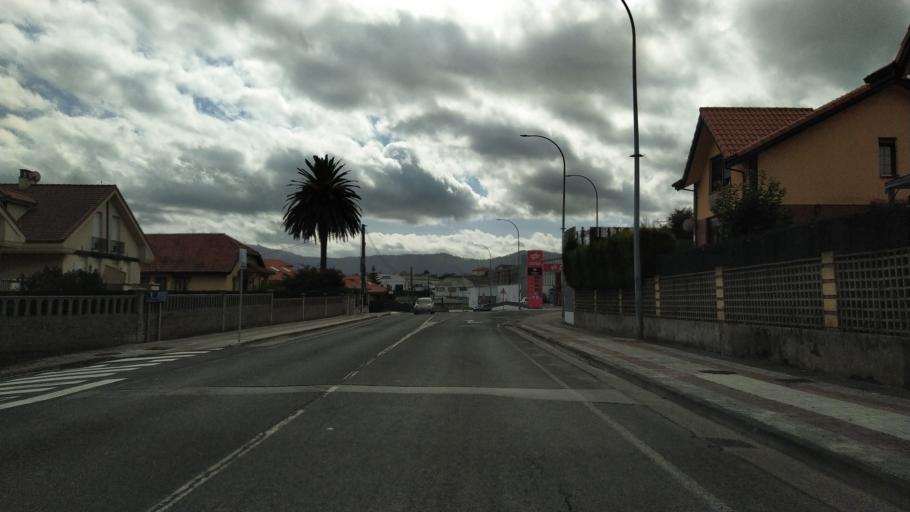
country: ES
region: Cantabria
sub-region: Provincia de Cantabria
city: Camargo
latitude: 43.4237
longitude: -3.8532
